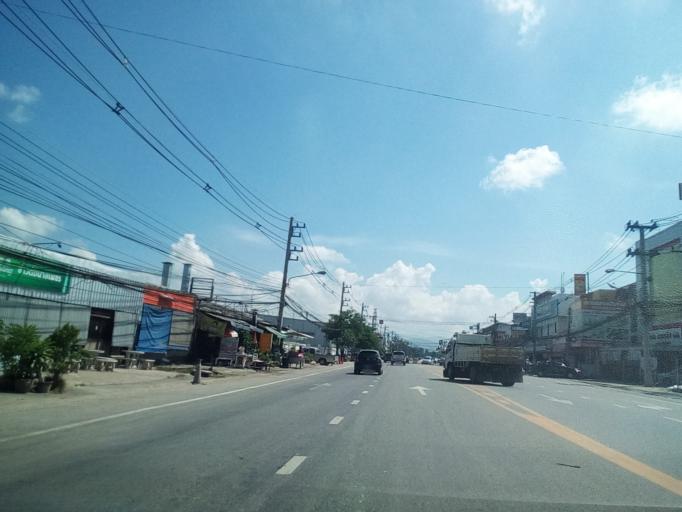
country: TH
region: Lamphun
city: Lamphun
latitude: 18.5876
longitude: 99.0478
